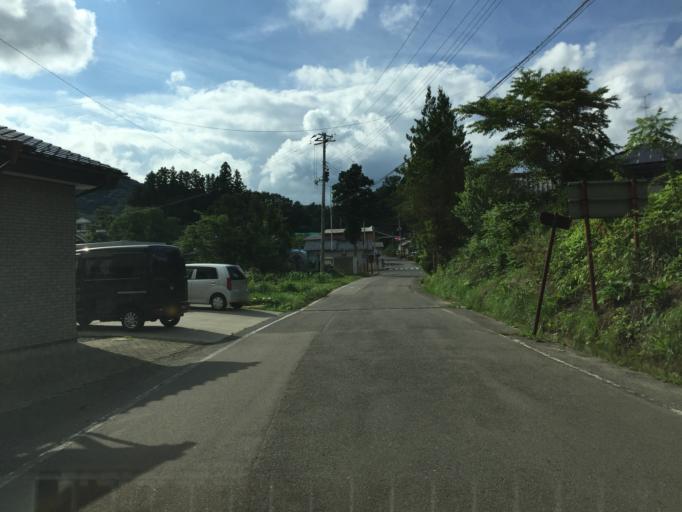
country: JP
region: Fukushima
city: Fukushima-shi
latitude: 37.6848
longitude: 140.5485
